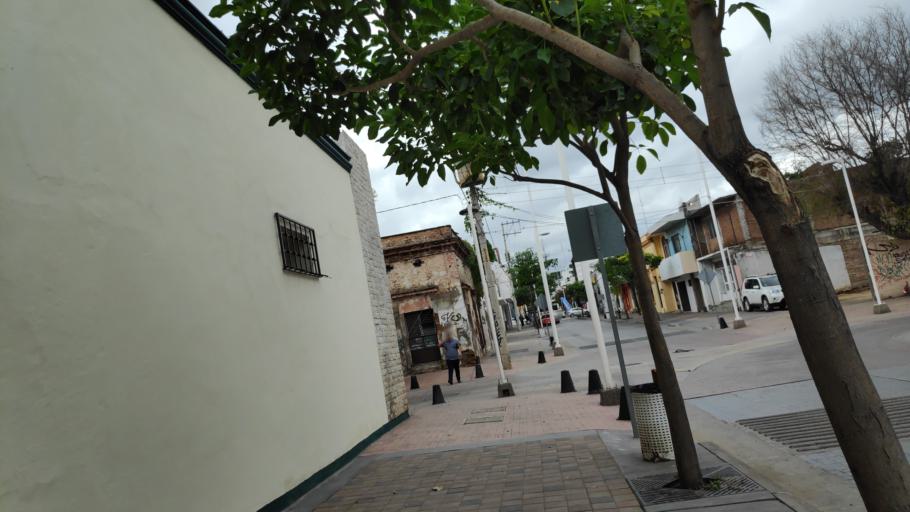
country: MX
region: Sinaloa
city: Culiacan
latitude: 24.8068
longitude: -107.3911
